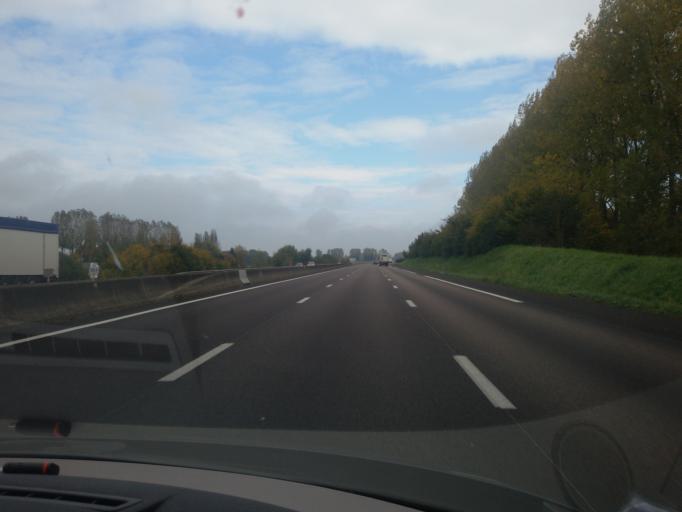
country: FR
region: Haute-Normandie
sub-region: Departement de l'Eure
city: Hauville
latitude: 49.3698
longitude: 0.7553
